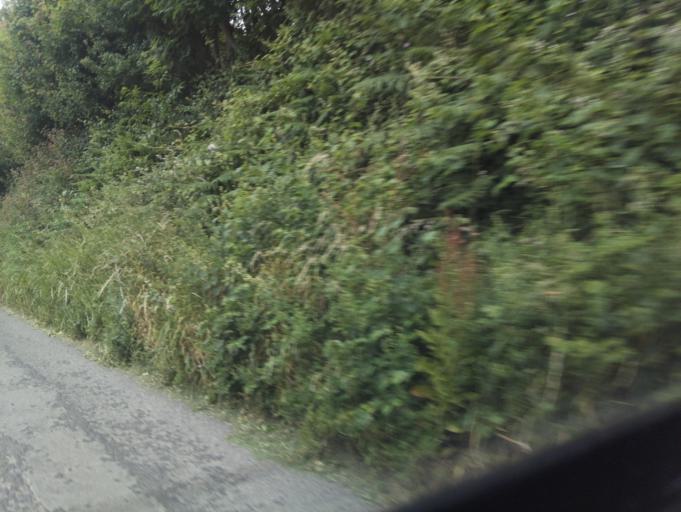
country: GB
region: England
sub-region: Dorset
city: Bridport
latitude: 50.7263
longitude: -2.7721
